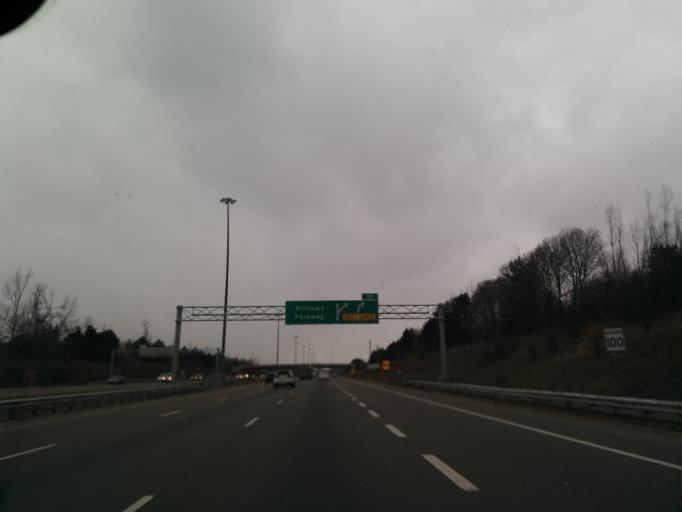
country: CA
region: Ontario
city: Brampton
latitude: 43.7097
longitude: -79.7437
